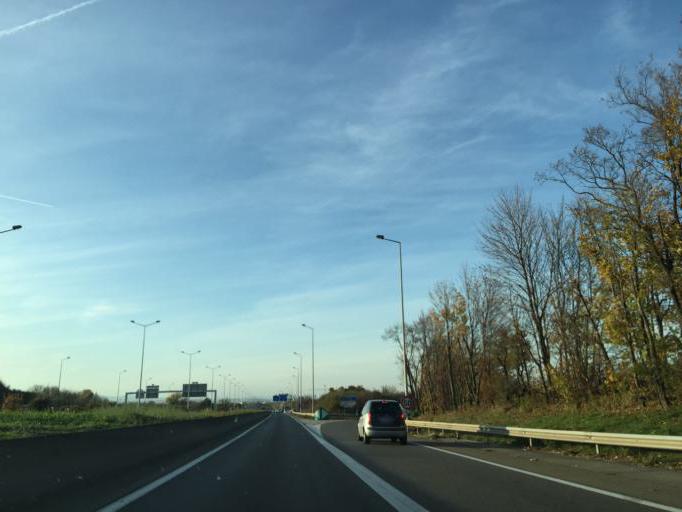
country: FR
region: Rhone-Alpes
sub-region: Departement du Rhone
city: Saint-Priest
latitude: 45.7017
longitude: 4.9695
